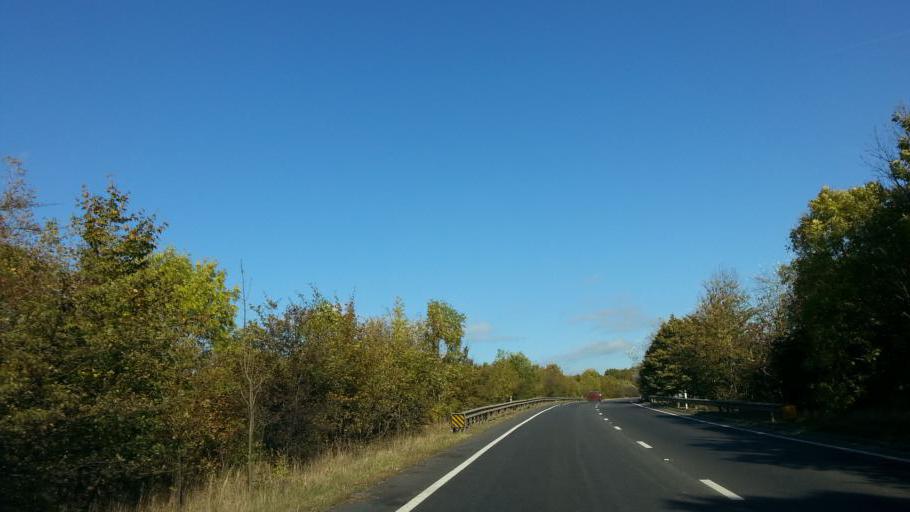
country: GB
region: England
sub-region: Northamptonshire
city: Stanwick
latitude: 52.3440
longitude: -0.5677
